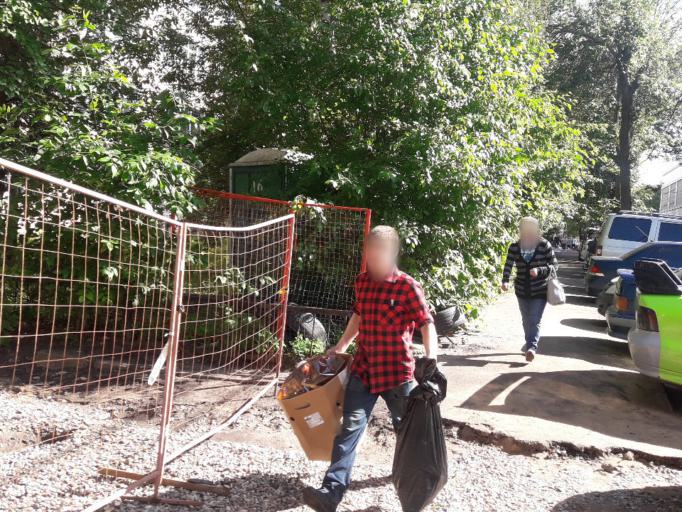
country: RU
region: Jaroslavl
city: Yaroslavl
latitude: 57.6275
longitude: 39.8733
